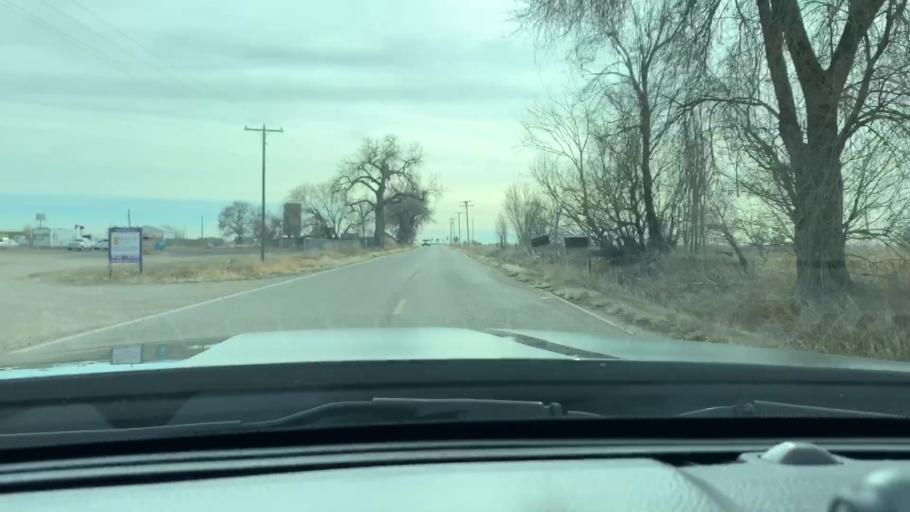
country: US
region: Colorado
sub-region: Weld County
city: Johnstown
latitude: 40.3522
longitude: -104.9835
